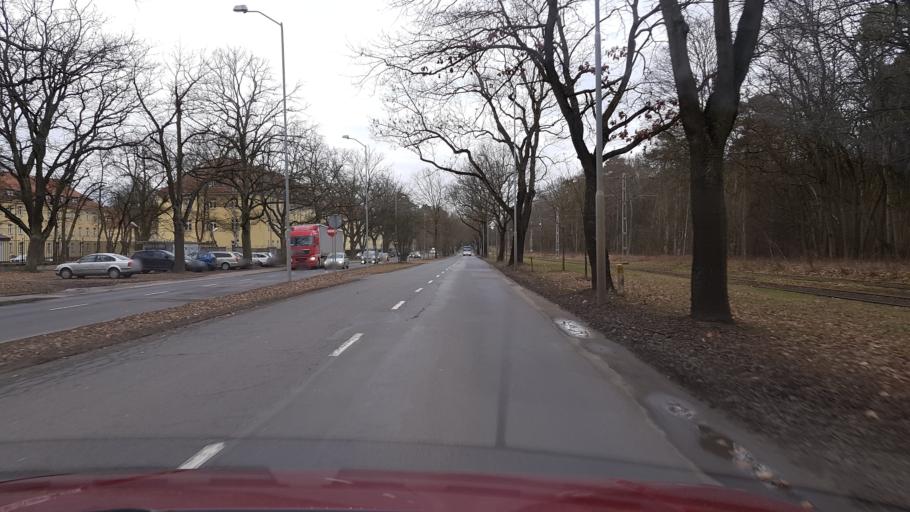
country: PL
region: West Pomeranian Voivodeship
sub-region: Szczecin
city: Szczecin
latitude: 53.4630
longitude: 14.4955
